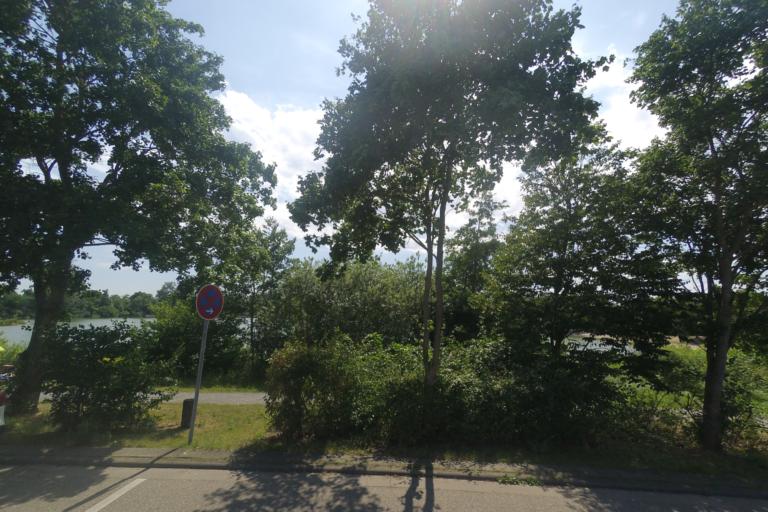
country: DE
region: Rheinland-Pfalz
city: Neuhofen
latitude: 49.4169
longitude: 8.4177
